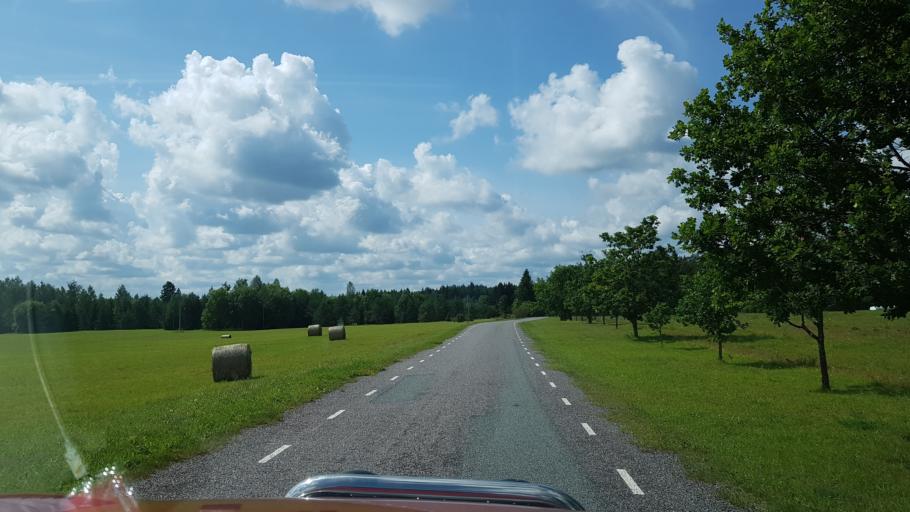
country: EE
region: Raplamaa
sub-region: Rapla vald
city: Rapla
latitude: 58.9655
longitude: 24.6165
